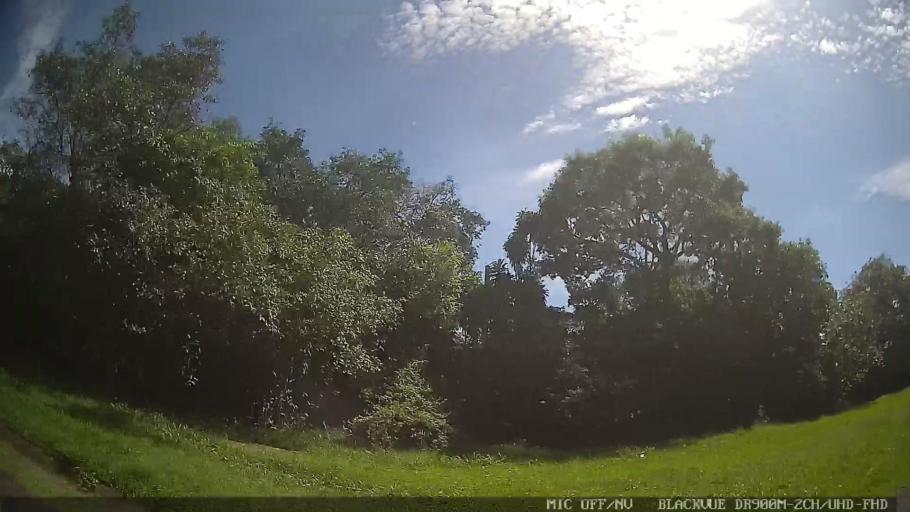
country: BR
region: Sao Paulo
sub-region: Tiete
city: Tiete
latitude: -23.1398
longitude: -47.6790
